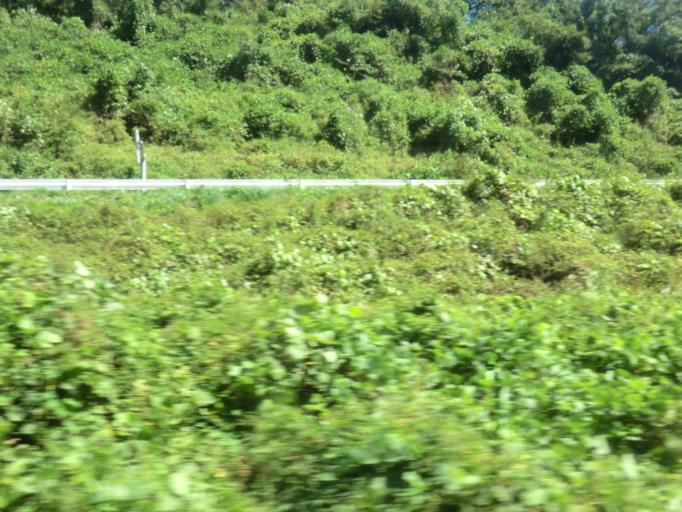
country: JP
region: Ibaraki
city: Iwase
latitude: 36.3509
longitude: 140.1655
